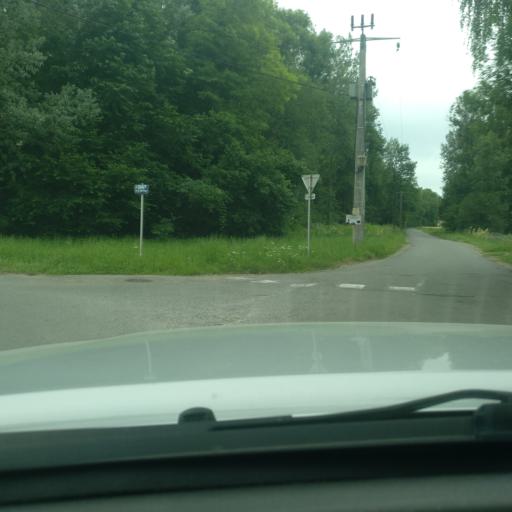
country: FR
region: Rhone-Alpes
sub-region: Departement de la Haute-Savoie
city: Amancy
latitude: 46.0830
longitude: 6.3464
